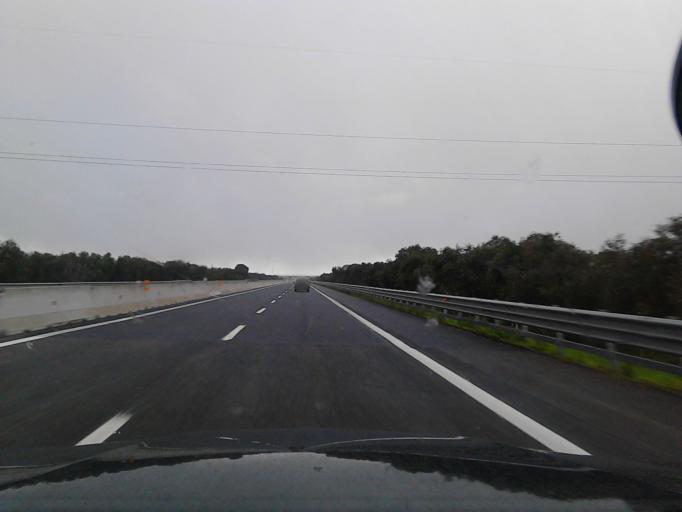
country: IT
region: Apulia
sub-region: Provincia di Bari
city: Giovinazzo
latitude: 41.1528
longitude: 16.6554
